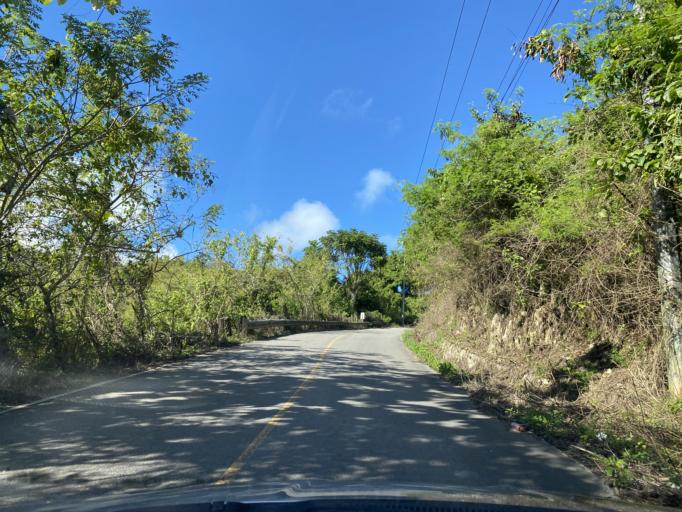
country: DO
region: Samana
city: Sanchez
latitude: 19.2466
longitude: -69.5959
